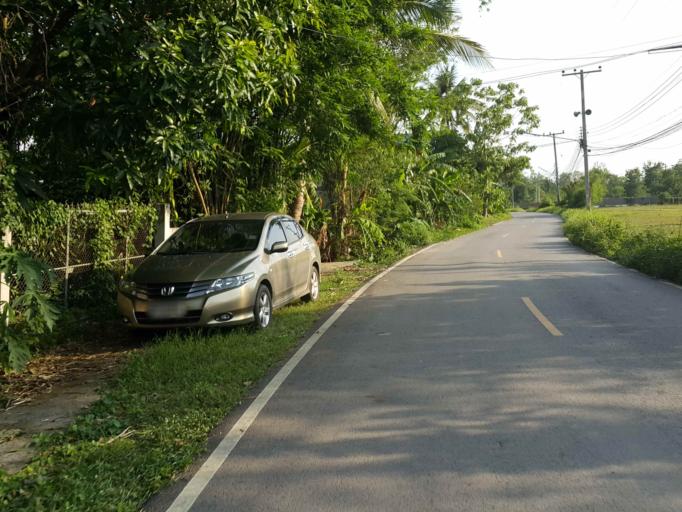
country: TH
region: Chiang Mai
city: San Sai
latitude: 18.8376
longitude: 99.1020
